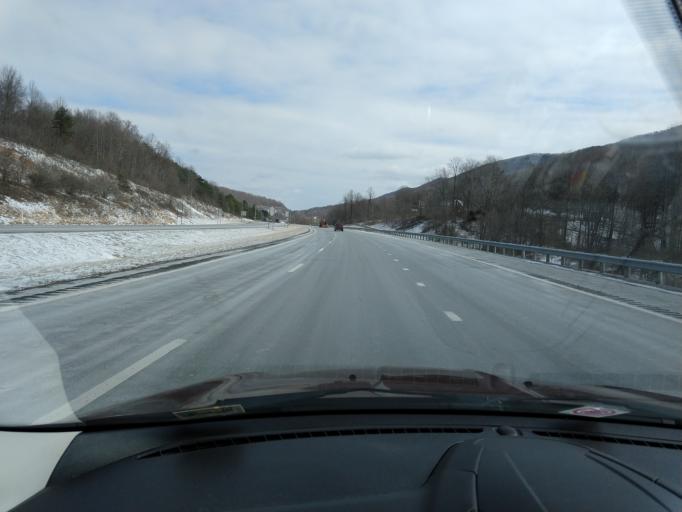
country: US
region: West Virginia
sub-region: Mercer County
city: Bluefield
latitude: 37.2734
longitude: -81.1600
